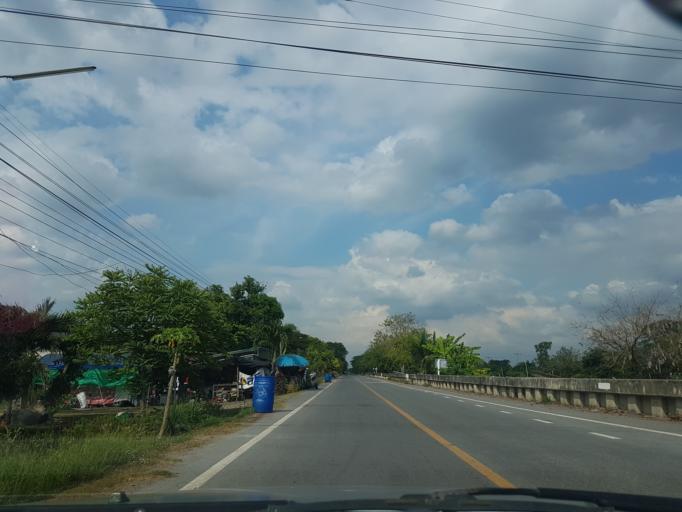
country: TH
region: Pathum Thani
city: Nong Suea
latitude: 14.1778
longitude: 100.8915
